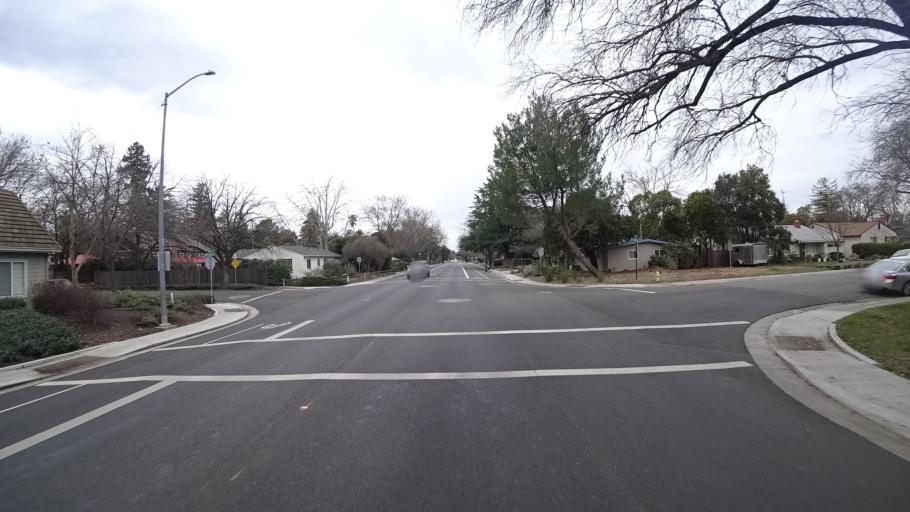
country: US
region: California
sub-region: Yolo County
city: Davis
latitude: 38.5507
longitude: -121.7500
